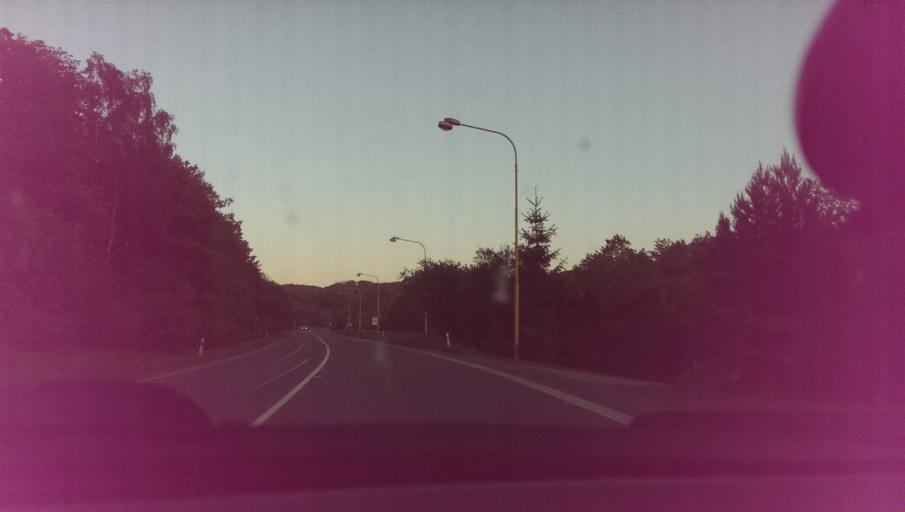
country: CZ
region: Zlin
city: Jablunka
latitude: 49.4267
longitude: 17.9575
